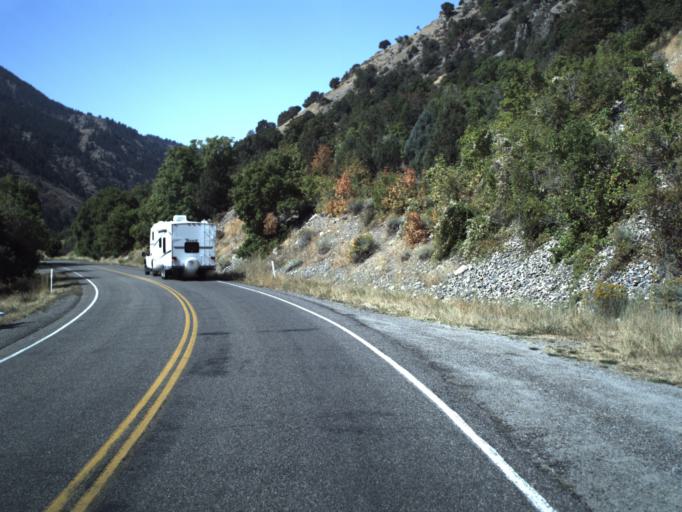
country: US
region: Utah
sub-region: Cache County
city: Millville
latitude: 41.6241
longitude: -111.7361
